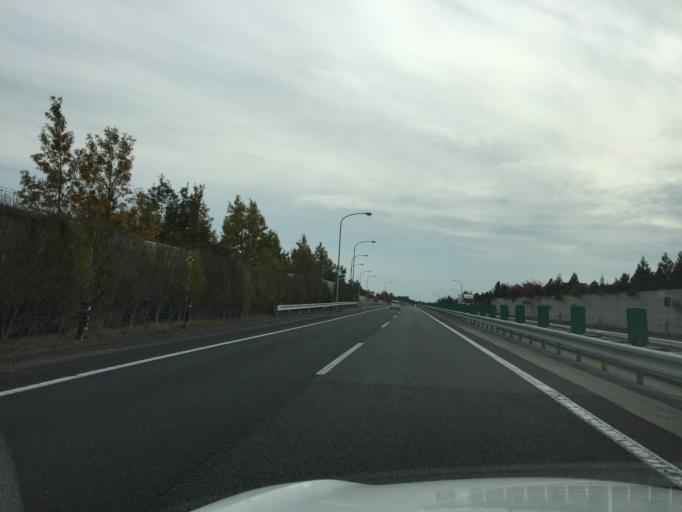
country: JP
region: Fukushima
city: Koriyama
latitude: 37.3903
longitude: 140.3114
